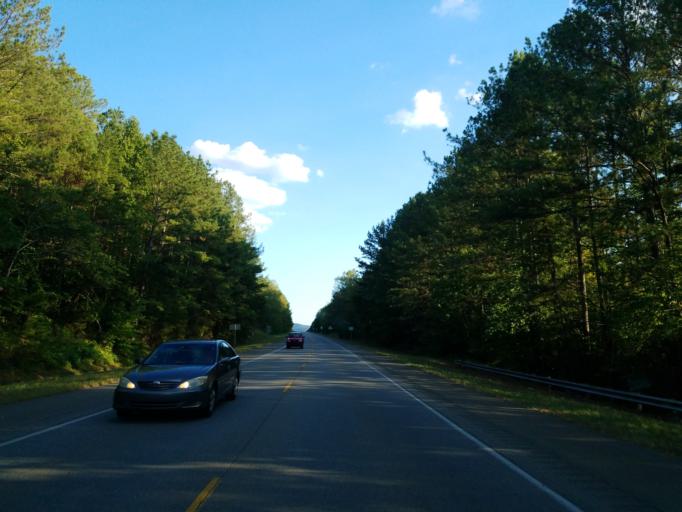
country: US
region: Georgia
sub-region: Murray County
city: Chatsworth
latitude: 34.5996
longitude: -84.7110
